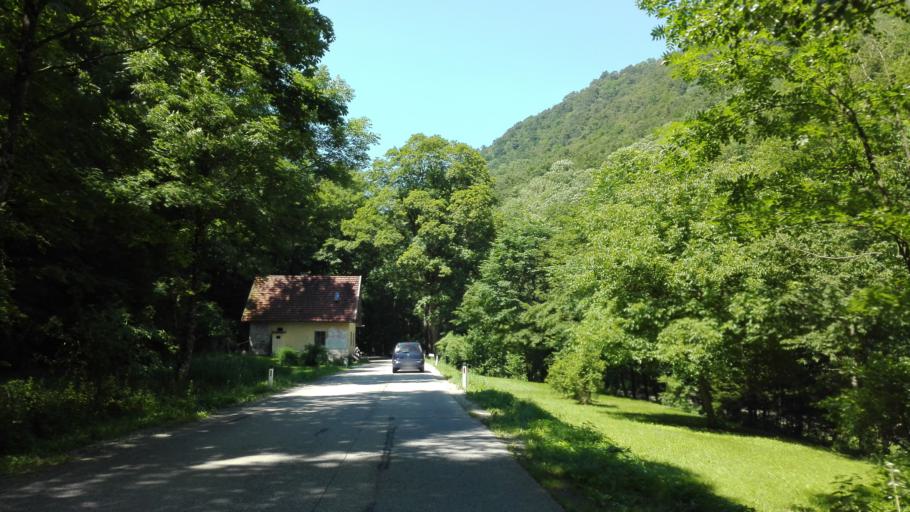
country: AT
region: Upper Austria
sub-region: Politischer Bezirk Rohrbach
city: Kleinzell im Muehlkreis
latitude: 48.3786
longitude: 13.9335
